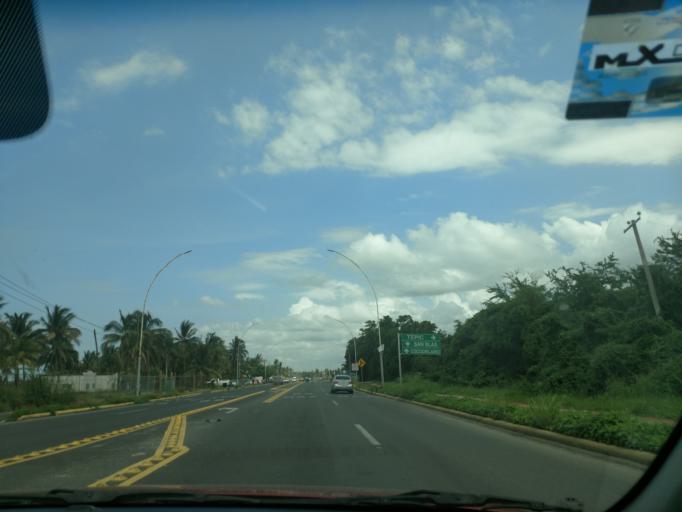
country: MX
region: Nayarit
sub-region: San Blas
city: Aticama
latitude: 21.5020
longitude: -105.2042
